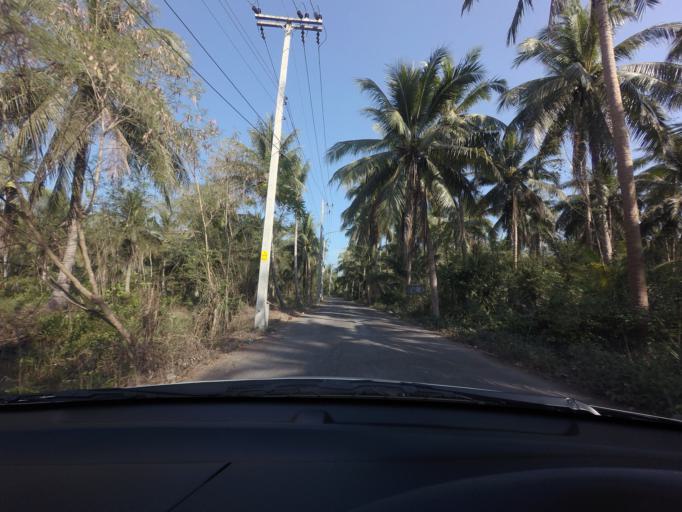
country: TH
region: Ratchaburi
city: Damnoen Saduak
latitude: 13.4836
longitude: 100.0022
